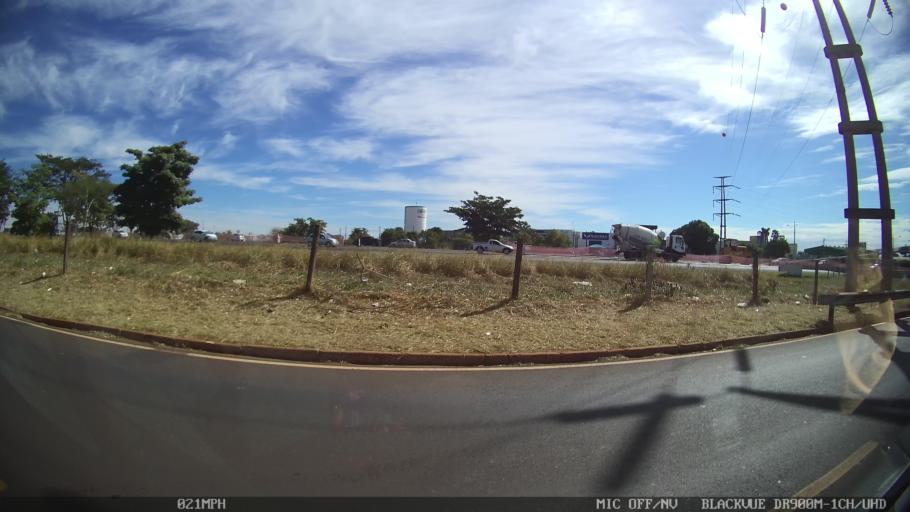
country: BR
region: Sao Paulo
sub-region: Sao Jose Do Rio Preto
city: Sao Jose do Rio Preto
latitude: -20.8291
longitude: -49.3599
